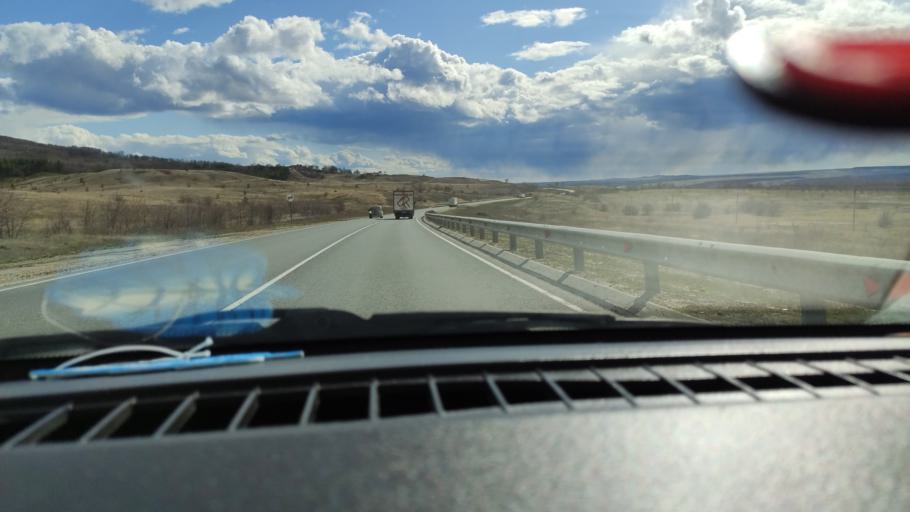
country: RU
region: Saratov
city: Alekseyevka
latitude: 52.3348
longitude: 47.9279
